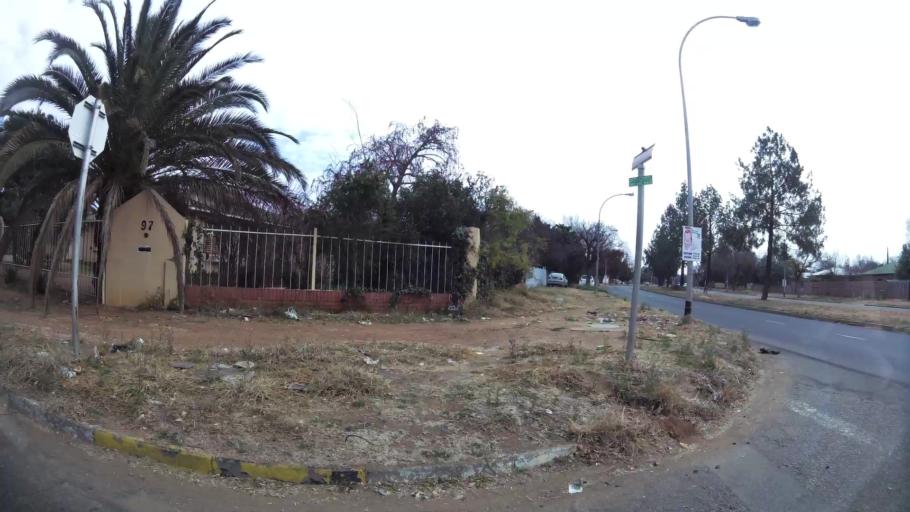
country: ZA
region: Orange Free State
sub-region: Mangaung Metropolitan Municipality
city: Bloemfontein
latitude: -29.1285
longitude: 26.1778
